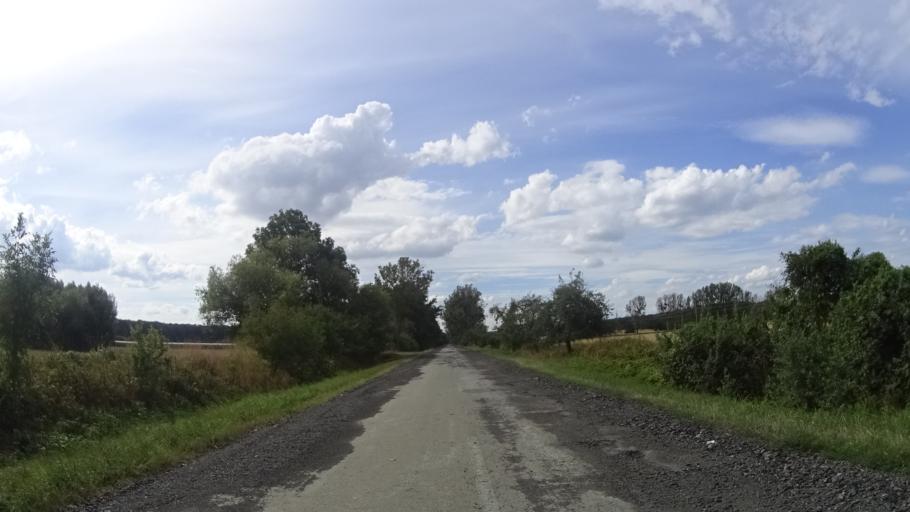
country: CZ
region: Olomoucky
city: Cervenka
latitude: 49.7150
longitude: 17.0519
